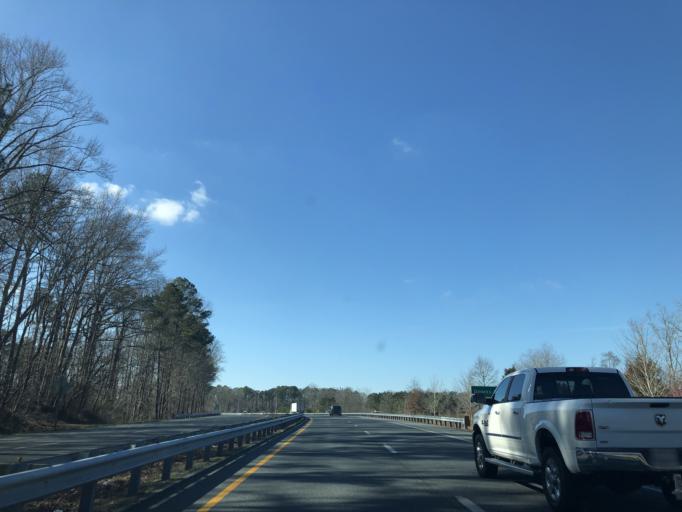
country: US
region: Maryland
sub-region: Worcester County
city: Berlin
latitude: 38.2653
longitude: -75.2502
